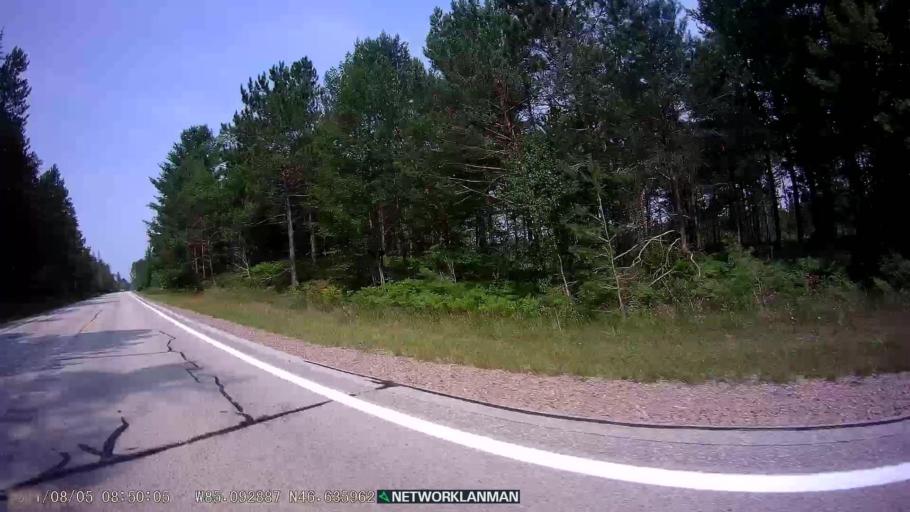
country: US
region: Michigan
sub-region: Luce County
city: Newberry
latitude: 46.6359
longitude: -85.0939
